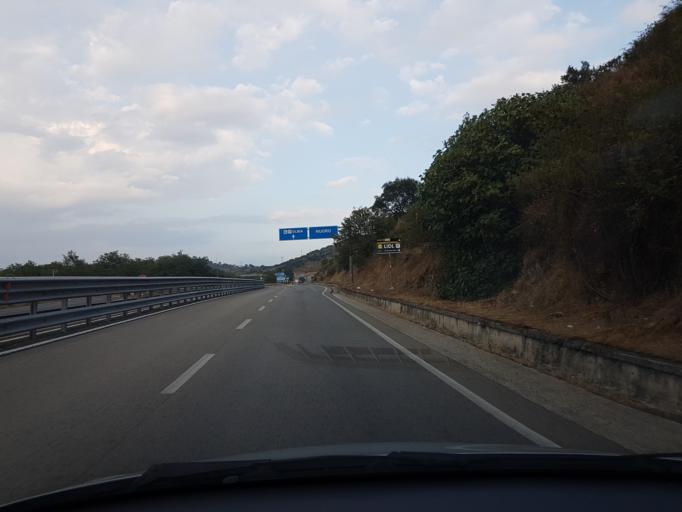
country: IT
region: Sardinia
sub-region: Provincia di Nuoro
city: Nuoro
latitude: 40.3227
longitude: 9.2763
